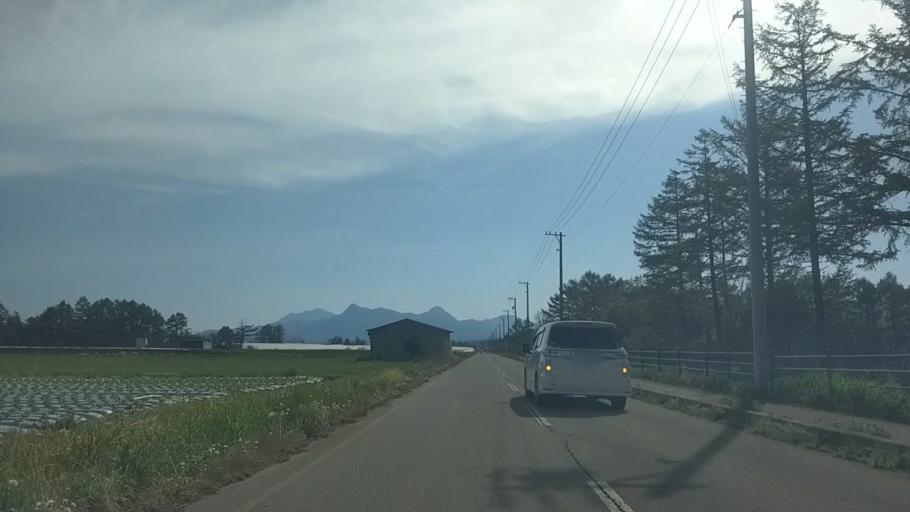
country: JP
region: Yamanashi
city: Nirasaki
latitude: 35.9479
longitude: 138.4612
